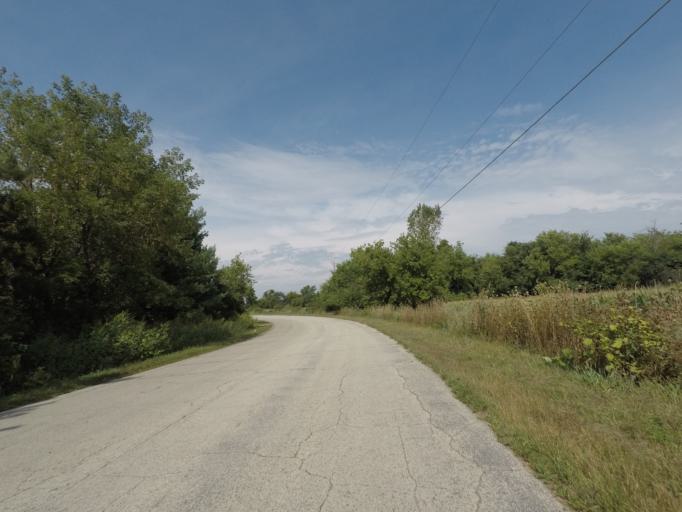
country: US
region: Wisconsin
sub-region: Jefferson County
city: Fort Atkinson
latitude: 42.8930
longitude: -88.8695
